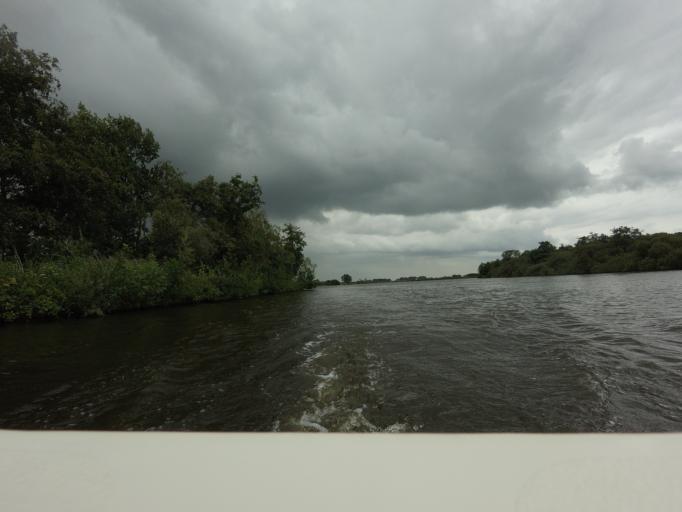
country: NL
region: Friesland
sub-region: Gemeente Tytsjerksteradiel
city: Garyp
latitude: 53.1211
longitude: 5.9441
